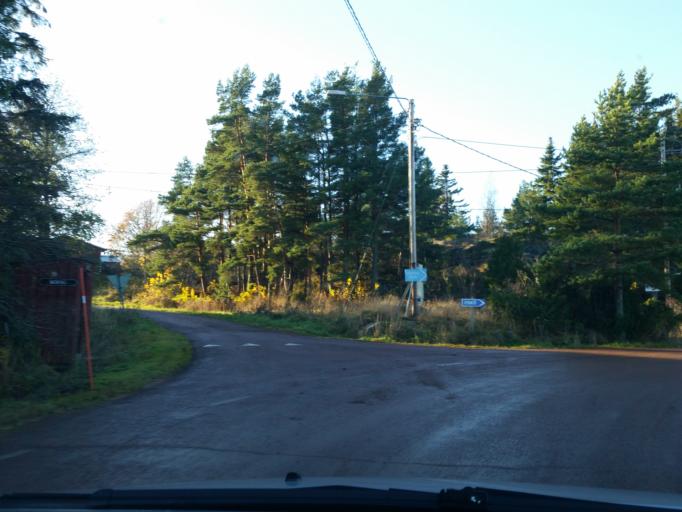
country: AX
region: Alands skaergard
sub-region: Braendoe
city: Braendoe
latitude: 60.4175
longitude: 20.9887
